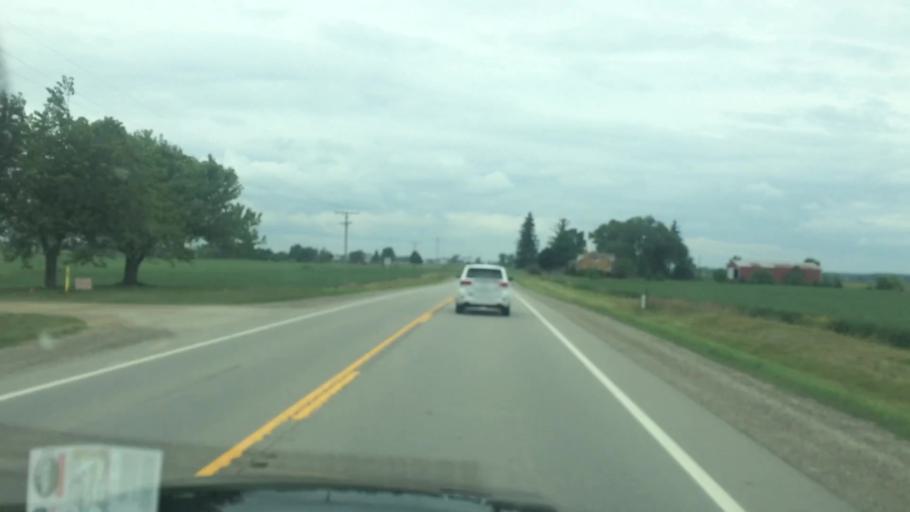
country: US
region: Michigan
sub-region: Sanilac County
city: Marlette
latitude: 43.3937
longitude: -83.0863
